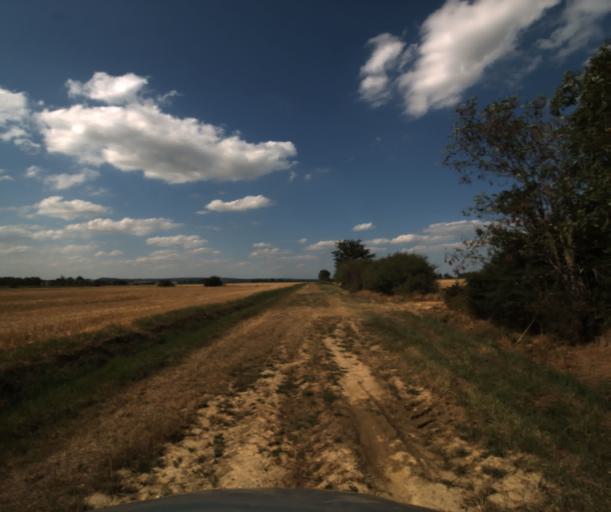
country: FR
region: Midi-Pyrenees
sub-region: Departement de la Haute-Garonne
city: Saint-Lys
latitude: 43.5195
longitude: 1.1771
